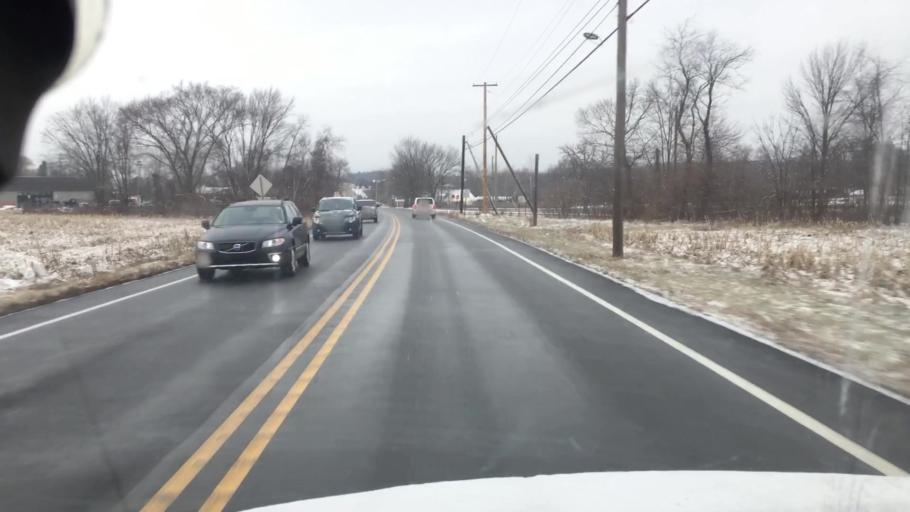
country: US
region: Pennsylvania
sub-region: Luzerne County
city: Nescopeck
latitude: 41.0426
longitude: -76.1422
